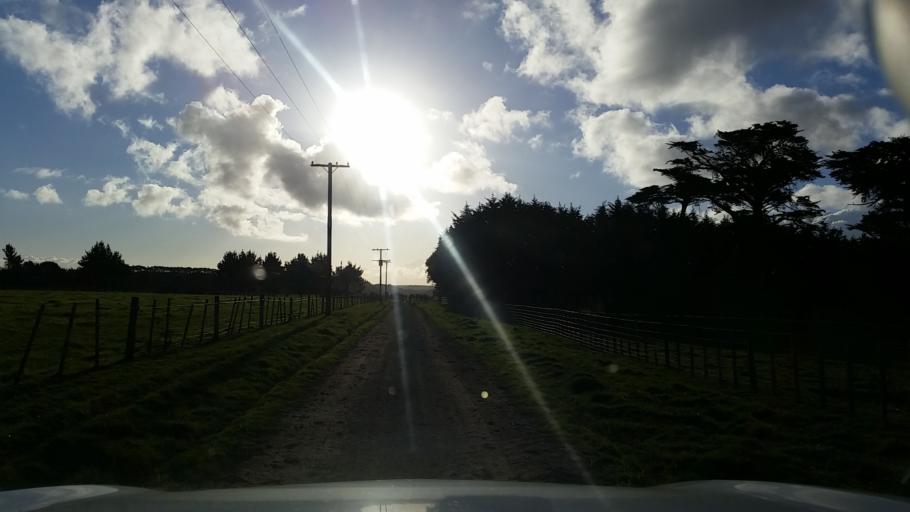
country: NZ
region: Taranaki
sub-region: South Taranaki District
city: Patea
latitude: -39.6154
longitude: 174.4937
